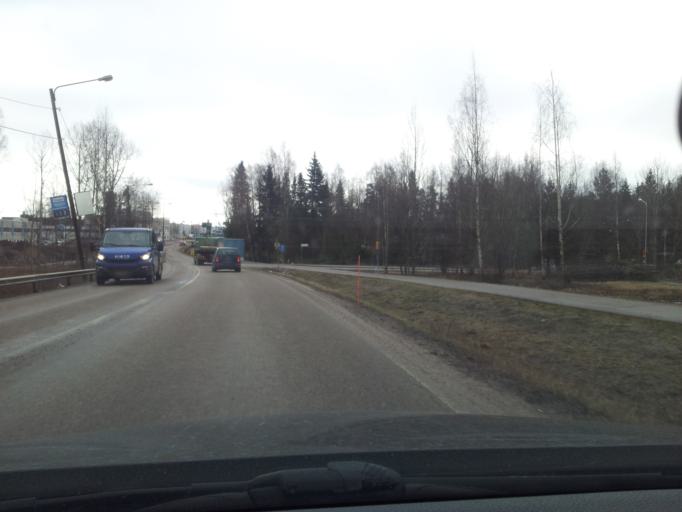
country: FI
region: Uusimaa
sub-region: Helsinki
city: Kauniainen
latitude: 60.1668
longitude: 24.6989
